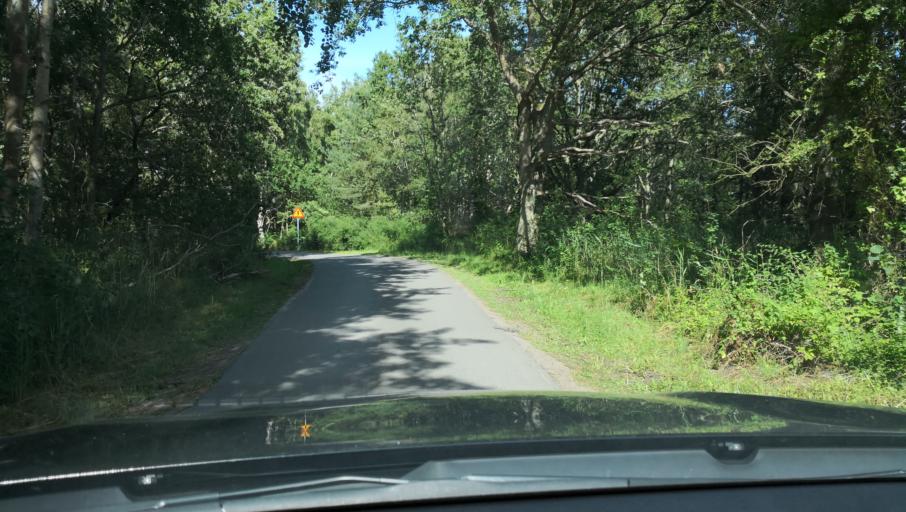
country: SE
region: Skane
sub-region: Ystads Kommun
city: Kopingebro
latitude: 55.3808
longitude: 14.1403
